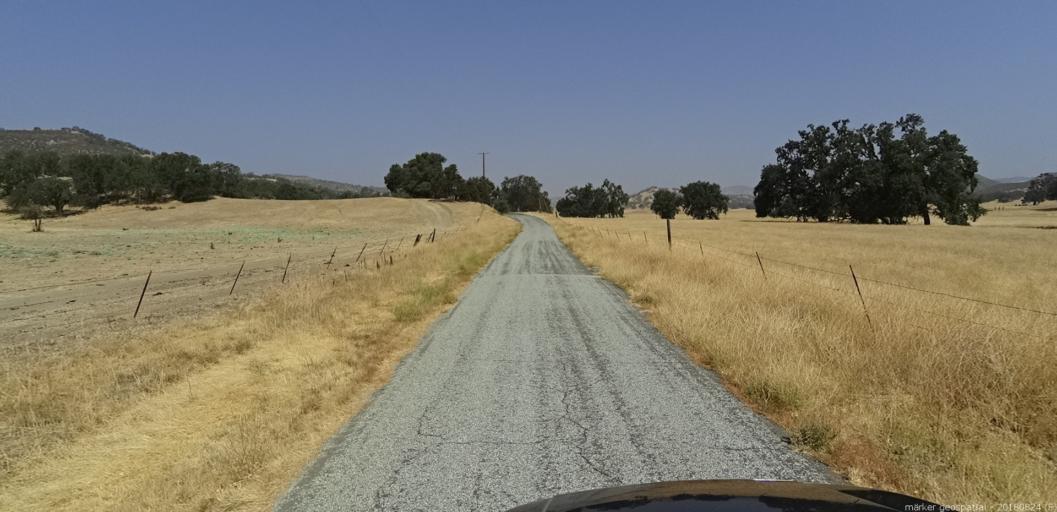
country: US
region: California
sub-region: San Luis Obispo County
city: San Miguel
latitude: 36.0263
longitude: -120.6546
